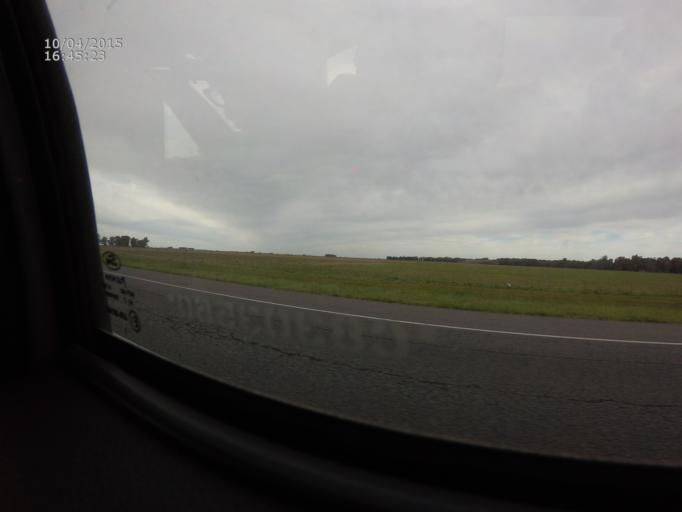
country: AR
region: Buenos Aires
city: Coronel Vidal
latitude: -37.7097
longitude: -57.6554
